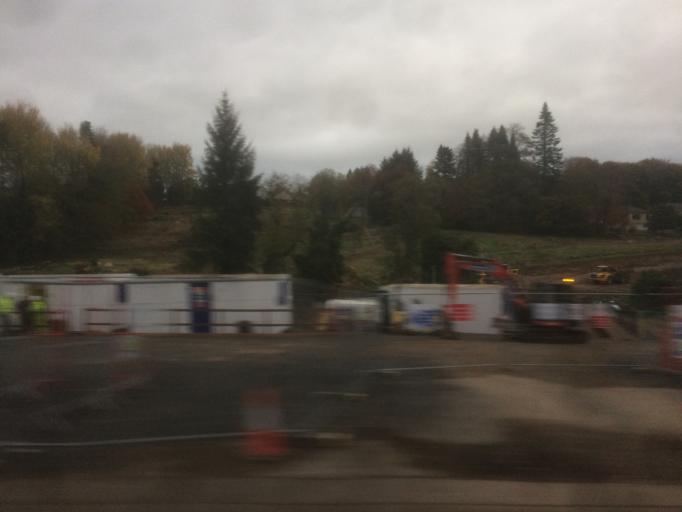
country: GB
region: Scotland
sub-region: Perth and Kinross
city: Perth
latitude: 56.3876
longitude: -3.4720
